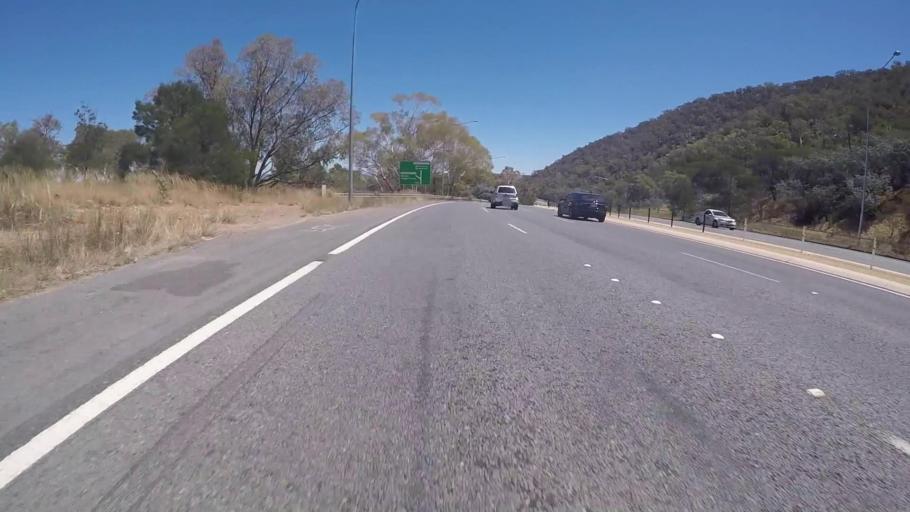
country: AU
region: Australian Capital Territory
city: Acton
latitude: -35.2853
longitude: 149.1010
